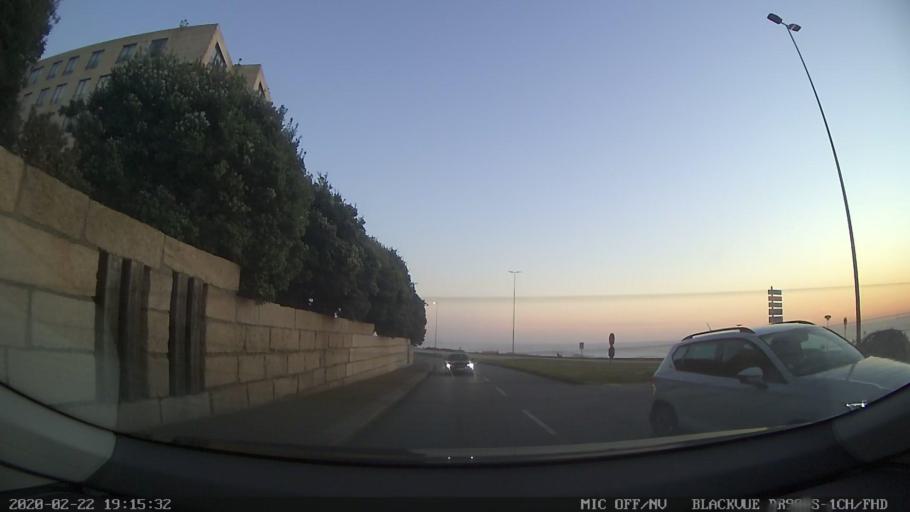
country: PT
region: Porto
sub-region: Matosinhos
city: Leca da Palmeira
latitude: 41.2004
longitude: -8.7111
